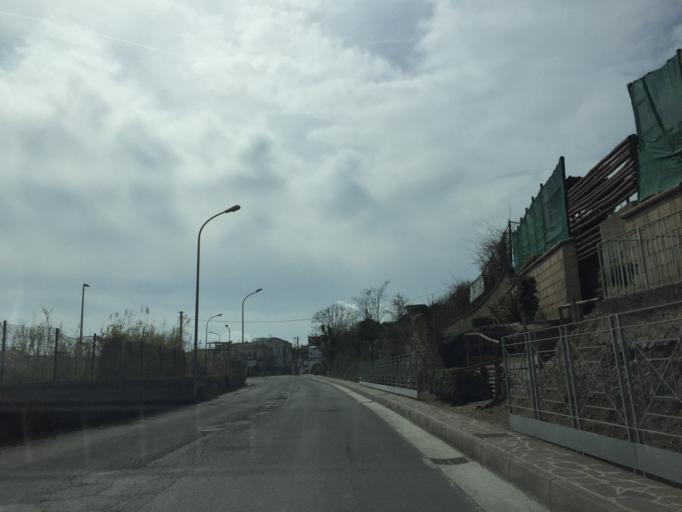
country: IT
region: Campania
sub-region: Provincia di Napoli
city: Bacoli
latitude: 40.7927
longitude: 14.0669
